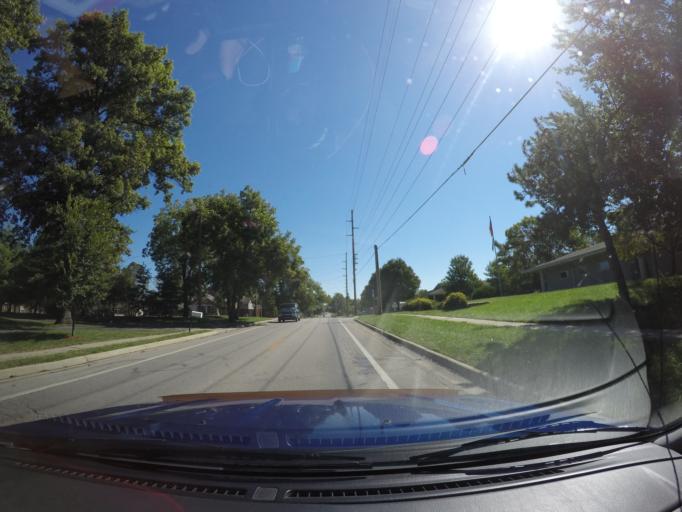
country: US
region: Kansas
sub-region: Douglas County
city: Lawrence
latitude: 38.9500
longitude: -95.2290
